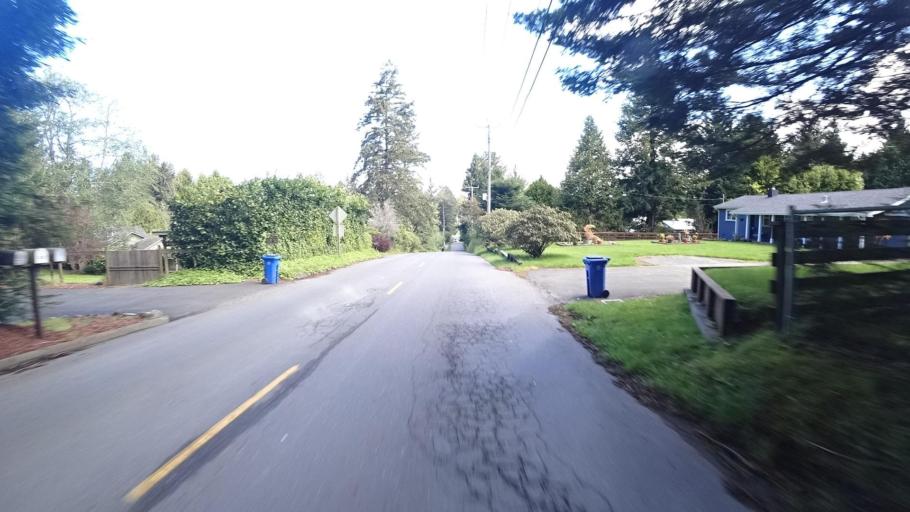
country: US
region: California
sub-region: Humboldt County
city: McKinleyville
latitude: 40.9240
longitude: -124.0816
